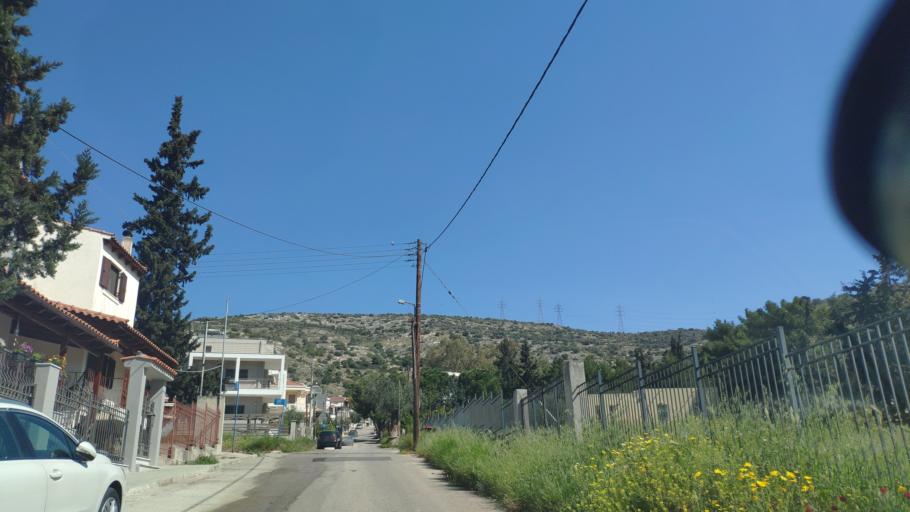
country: GR
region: Attica
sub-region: Nomarchia Athinas
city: Skaramangas
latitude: 38.0128
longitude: 23.6153
